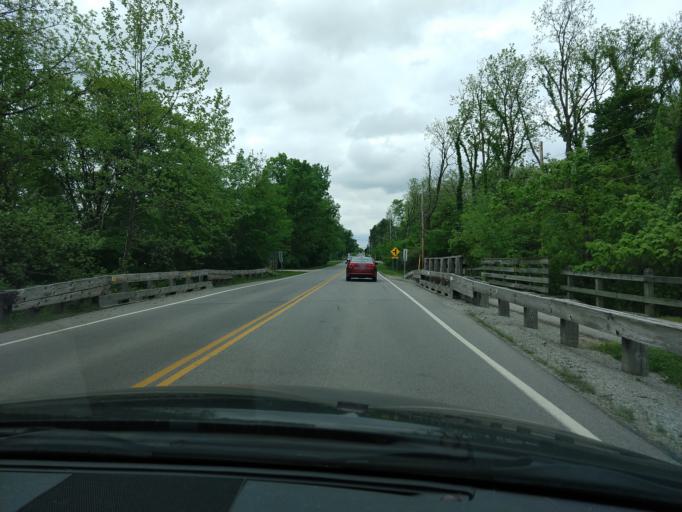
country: US
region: Indiana
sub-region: Hamilton County
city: Westfield
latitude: 40.0132
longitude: -86.1274
